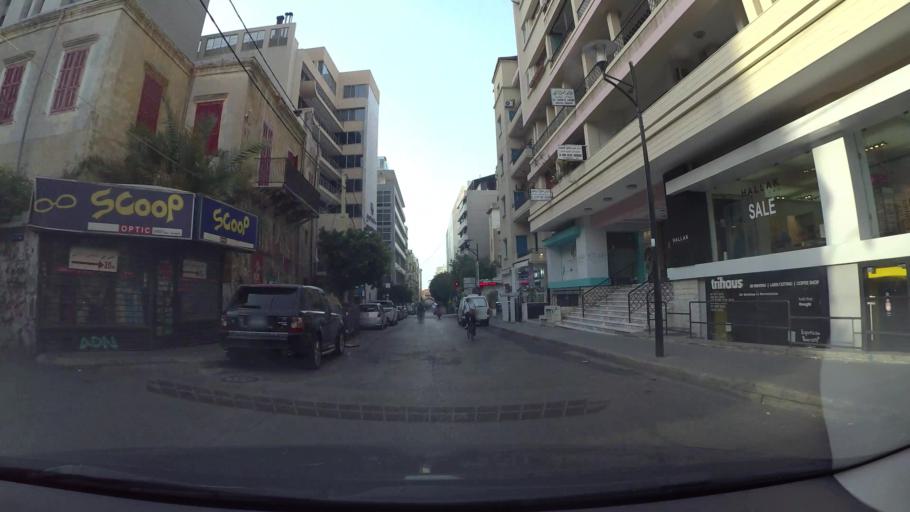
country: LB
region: Beyrouth
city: Ra's Bayrut
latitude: 33.8965
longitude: 35.4838
